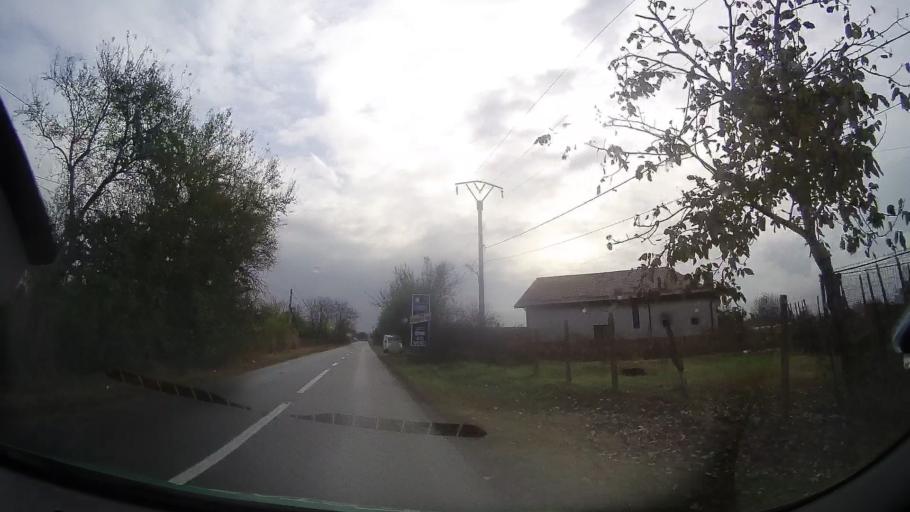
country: RO
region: Ialomita
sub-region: Comuna Fierbinti-Targ
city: Fierbintii de Jos
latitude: 44.6992
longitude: 26.3937
